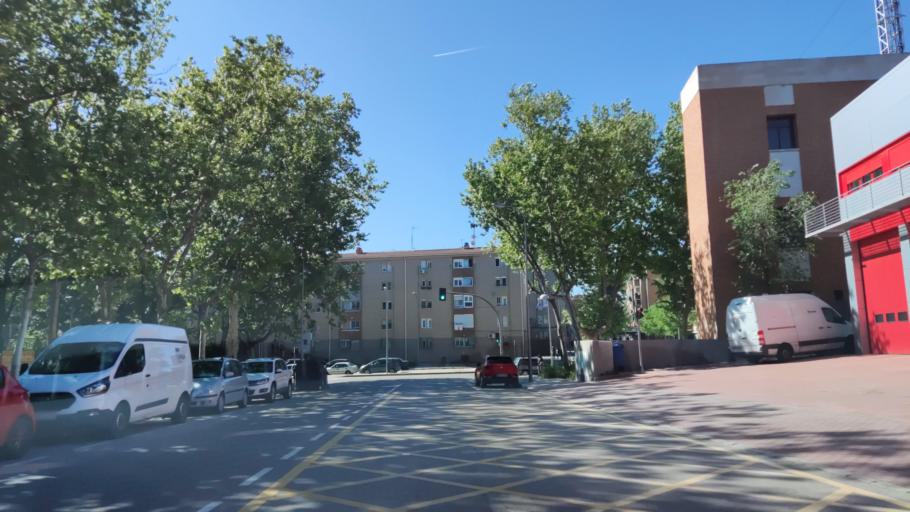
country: ES
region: Madrid
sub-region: Provincia de Madrid
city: San Blas
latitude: 40.4286
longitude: -3.6152
